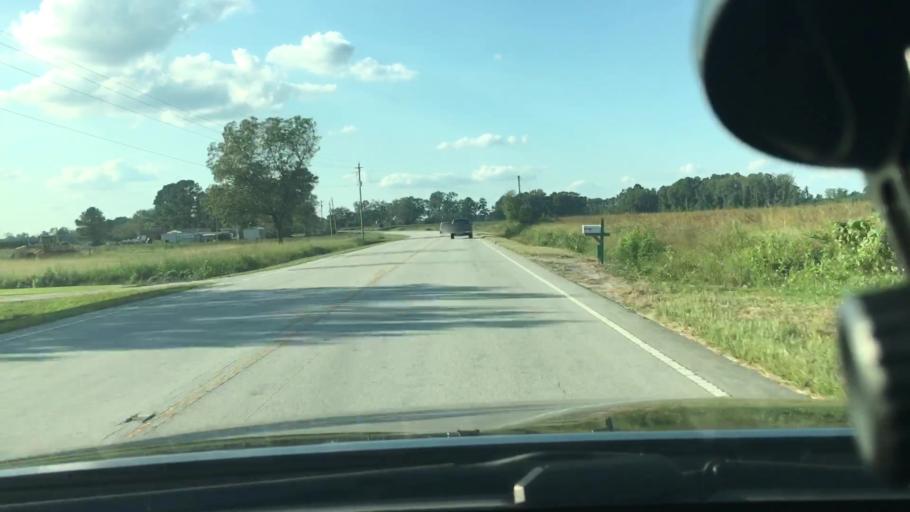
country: US
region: North Carolina
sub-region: Craven County
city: Vanceboro
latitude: 35.3718
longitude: -77.2079
